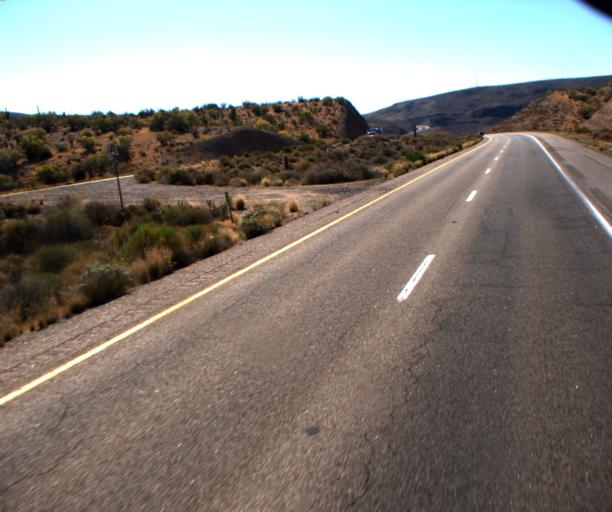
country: US
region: Arizona
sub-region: Yavapai County
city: Bagdad
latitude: 34.5880
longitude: -113.5089
